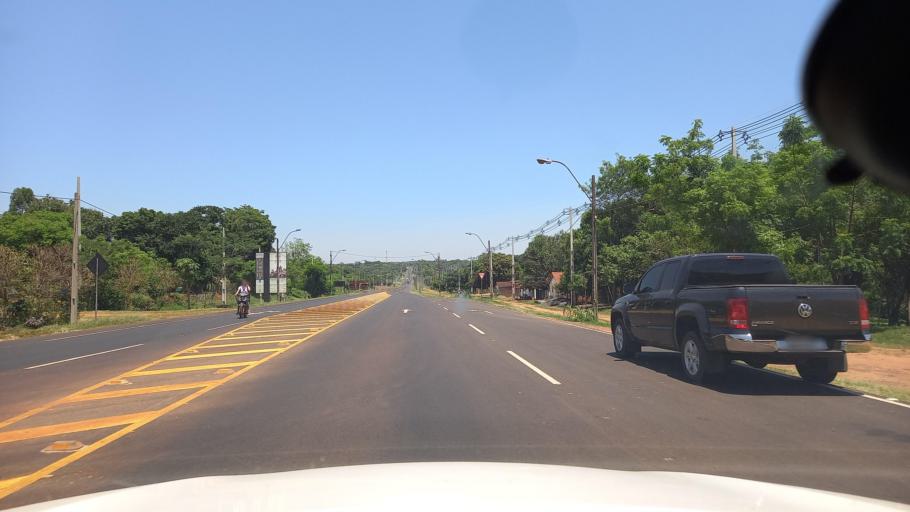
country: PY
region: Misiones
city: Santa Maria
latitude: -26.8740
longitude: -56.9900
